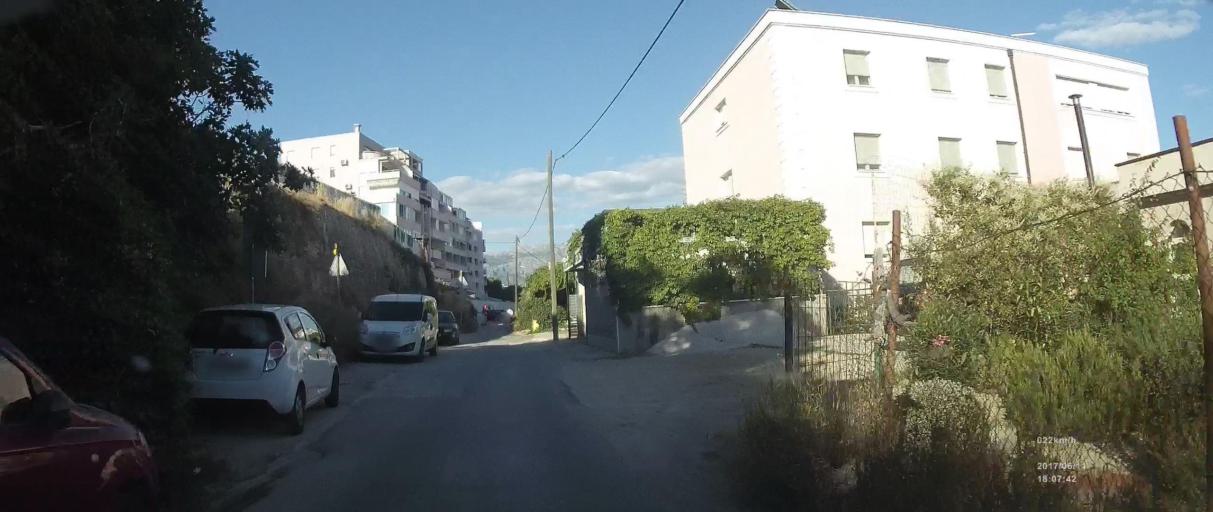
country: HR
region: Splitsko-Dalmatinska
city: Vranjic
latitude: 43.5032
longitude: 16.4724
